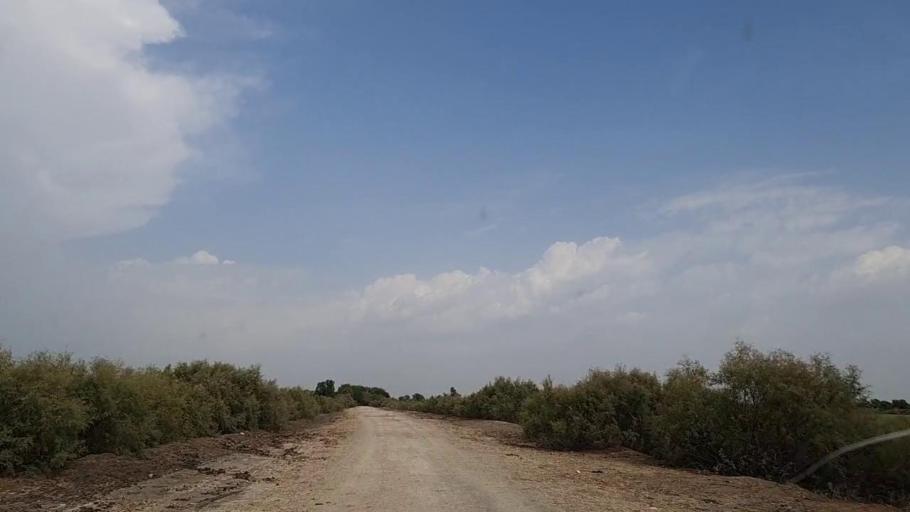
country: PK
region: Sindh
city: Khanpur
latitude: 27.8188
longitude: 69.5307
